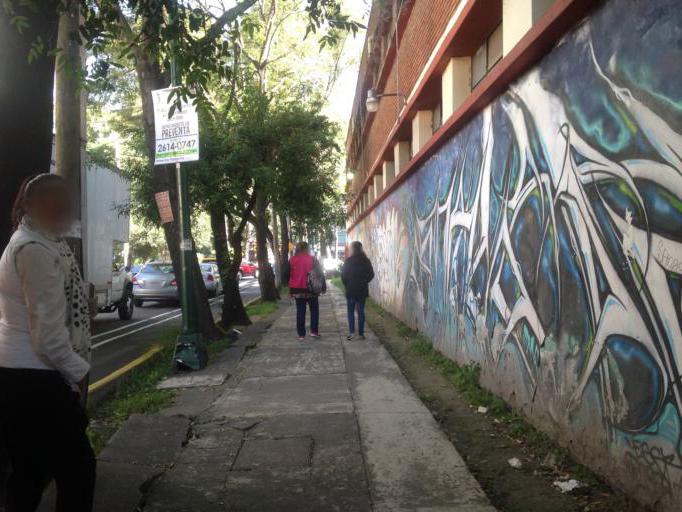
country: MX
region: Mexico City
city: Colonia del Valle
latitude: 19.3848
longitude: -99.1693
